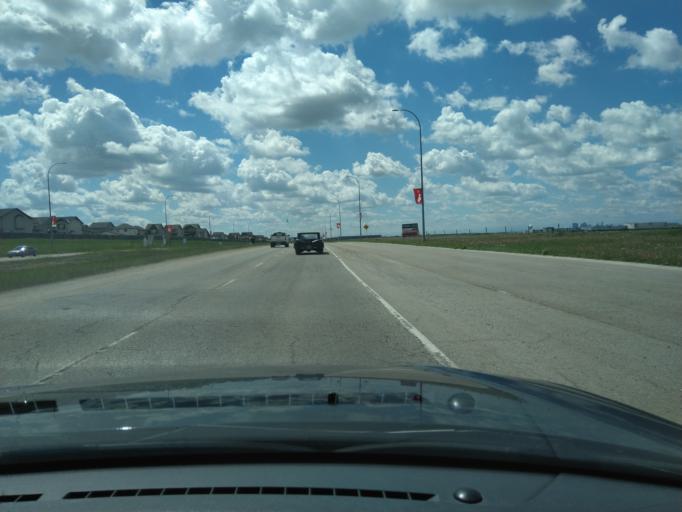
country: CA
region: Alberta
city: Airdrie
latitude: 51.1641
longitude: -113.9703
